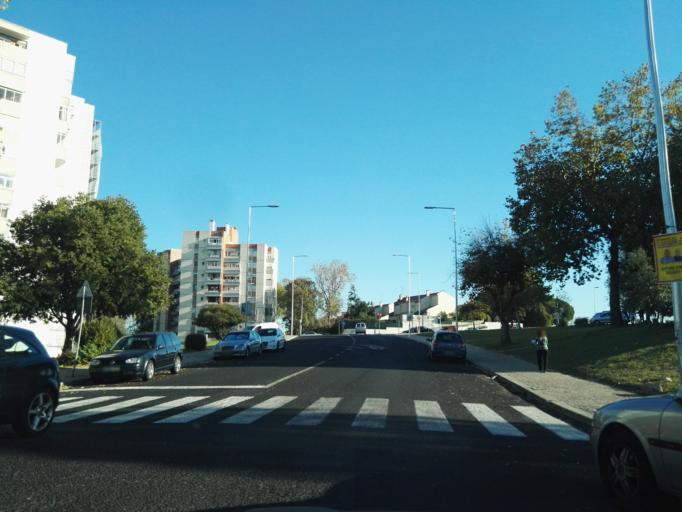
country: PT
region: Lisbon
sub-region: Loures
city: Moscavide
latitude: 38.7630
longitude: -9.1210
